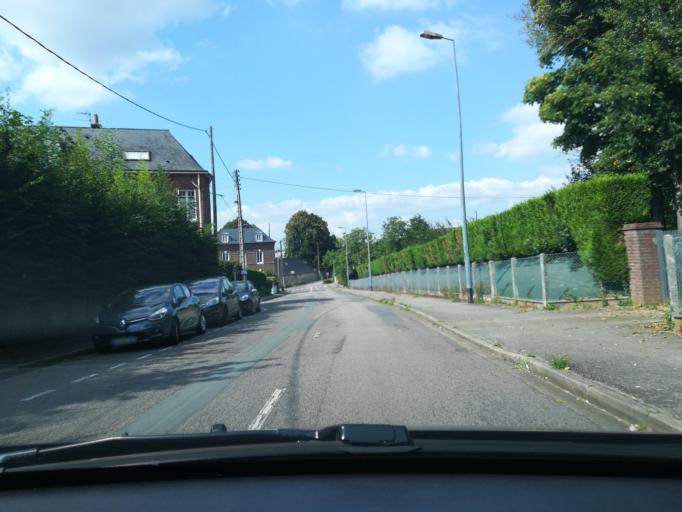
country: FR
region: Haute-Normandie
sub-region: Departement de la Seine-Maritime
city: Bois-Guillaume
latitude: 49.4655
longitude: 1.1086
